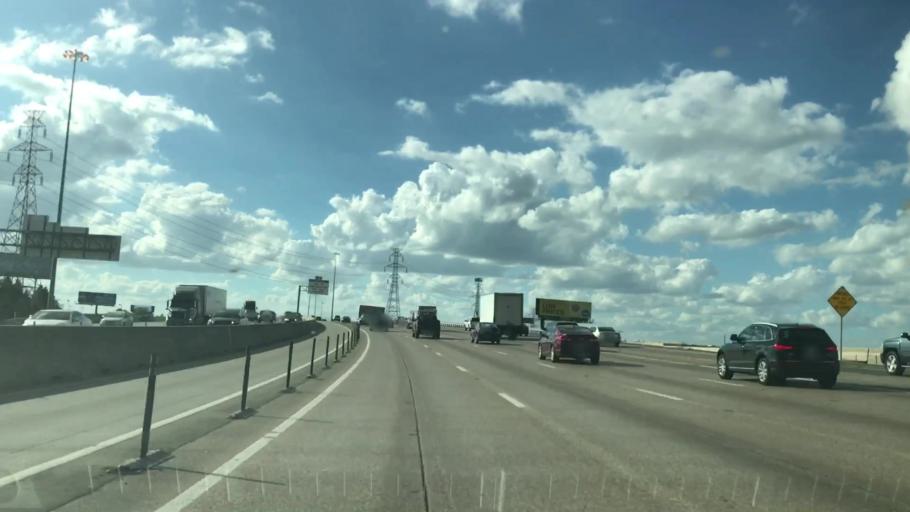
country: US
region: Texas
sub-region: Dallas County
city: Garland
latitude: 32.8698
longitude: -96.6706
